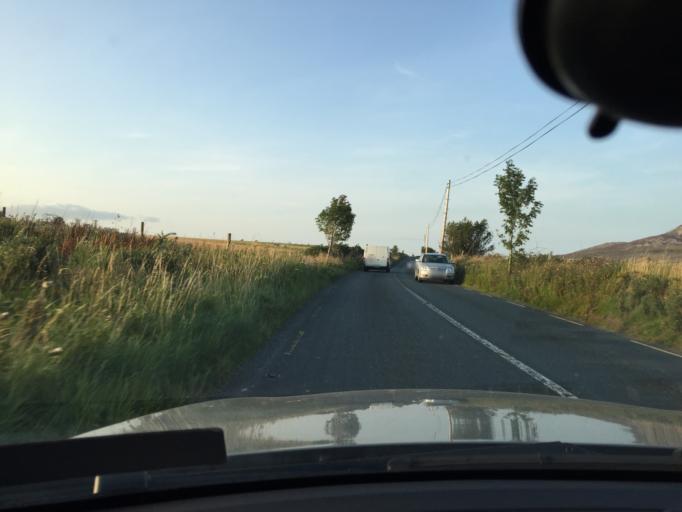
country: IE
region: Leinster
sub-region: Wicklow
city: Kilmacanoge
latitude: 53.1339
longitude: -6.1767
